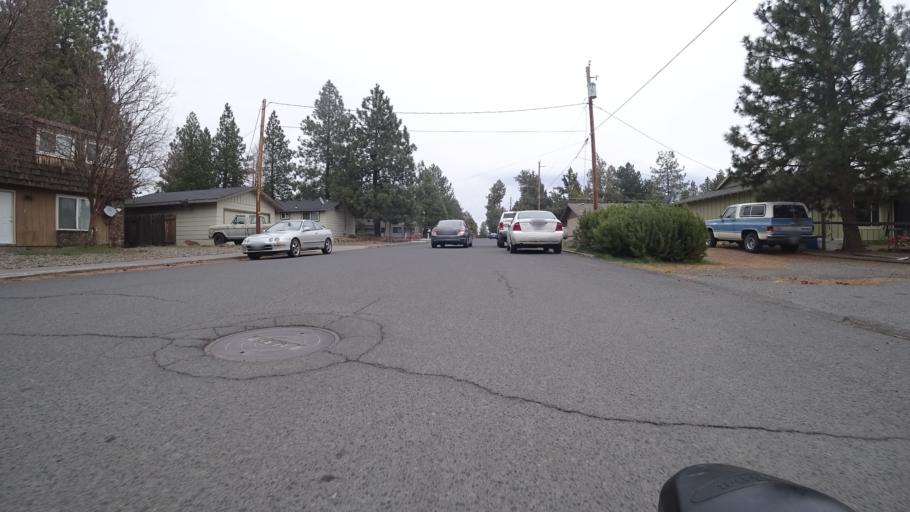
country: US
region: Oregon
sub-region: Deschutes County
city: Bend
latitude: 44.0460
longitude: -121.2829
